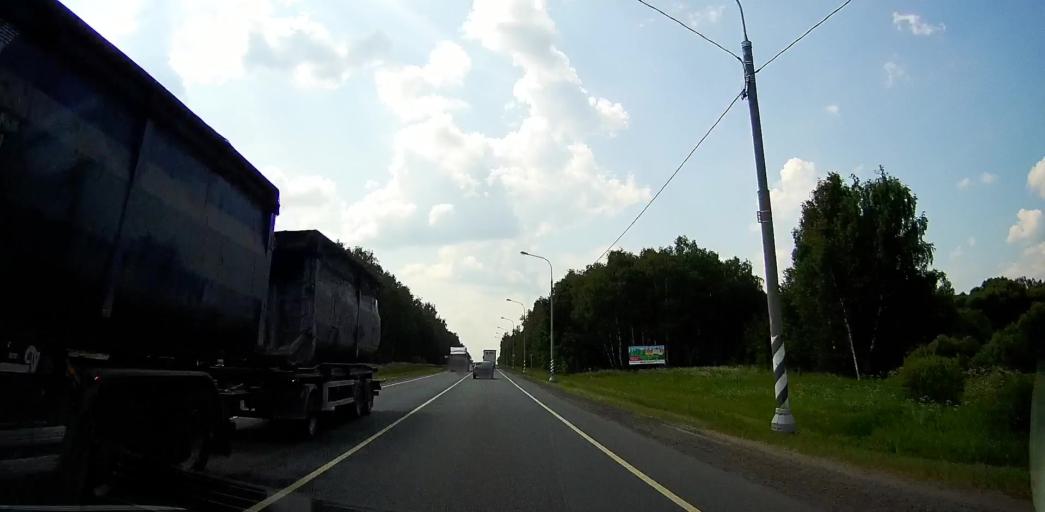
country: RU
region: Moskovskaya
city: Malino
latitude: 55.1251
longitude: 38.2334
